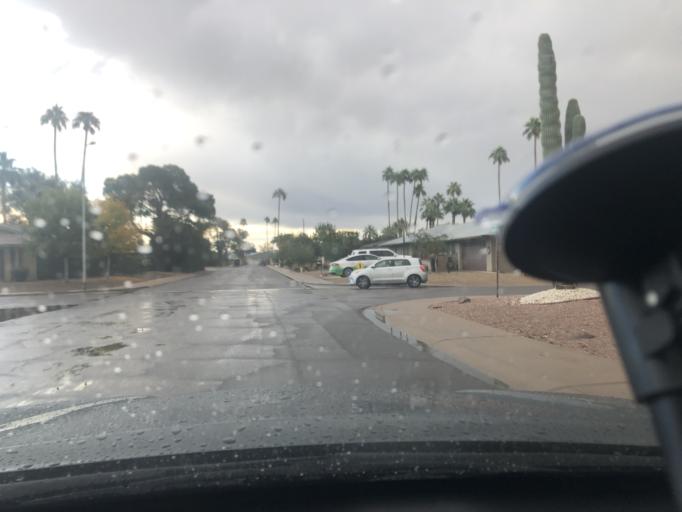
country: US
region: Arizona
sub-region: Maricopa County
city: Scottsdale
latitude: 33.4978
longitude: -111.8946
